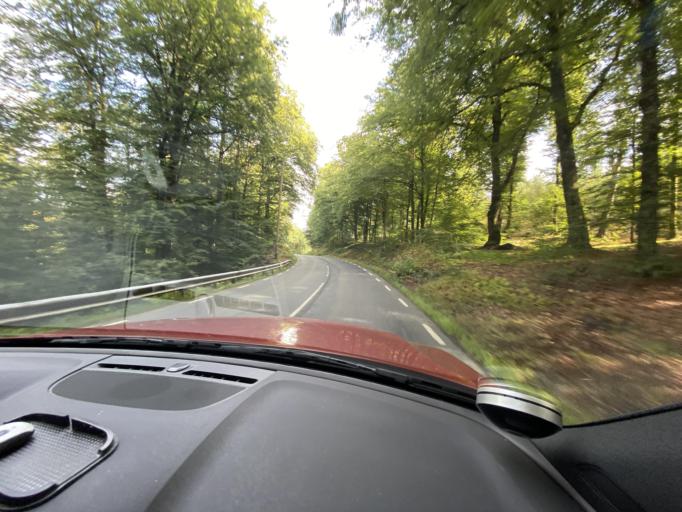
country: SE
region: Skane
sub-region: Hassleholms Kommun
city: Bjarnum
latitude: 56.3550
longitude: 13.7710
